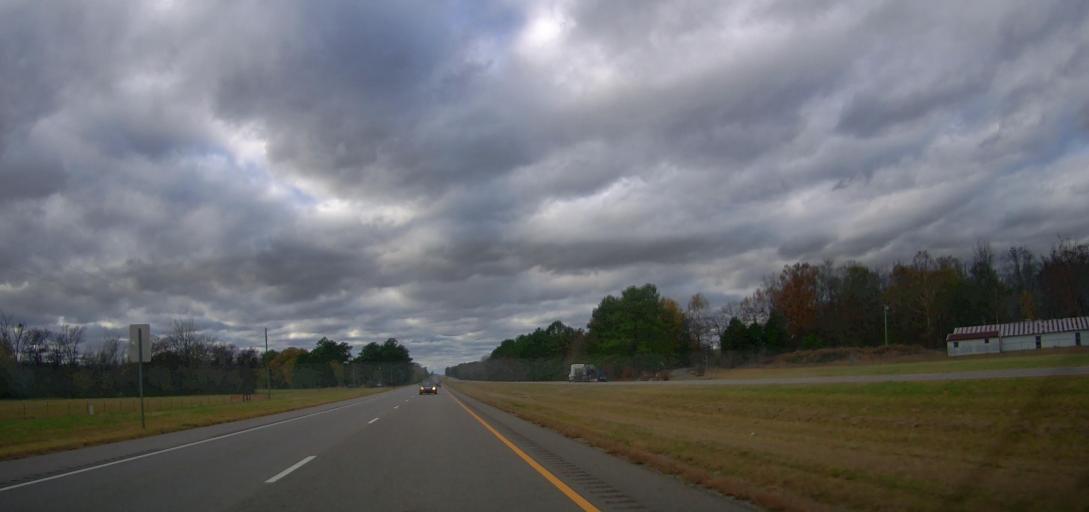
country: US
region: Alabama
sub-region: Morgan County
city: Danville
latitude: 34.3455
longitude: -87.0351
